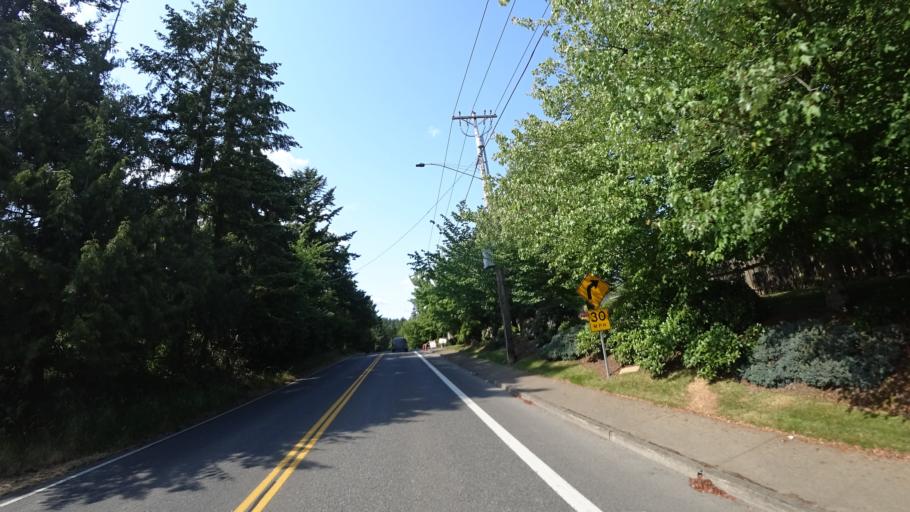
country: US
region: Oregon
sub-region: Clackamas County
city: Sunnyside
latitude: 45.4340
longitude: -122.5381
